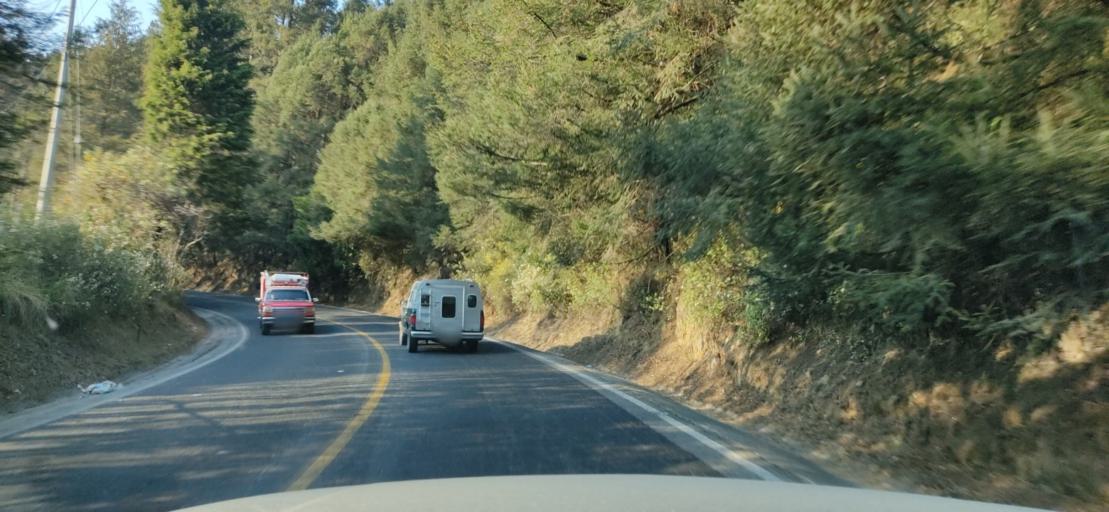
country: MX
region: Mexico
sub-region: Ocoyoacac
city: San Jeronimo Acazulco
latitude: 19.2619
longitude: -99.3715
